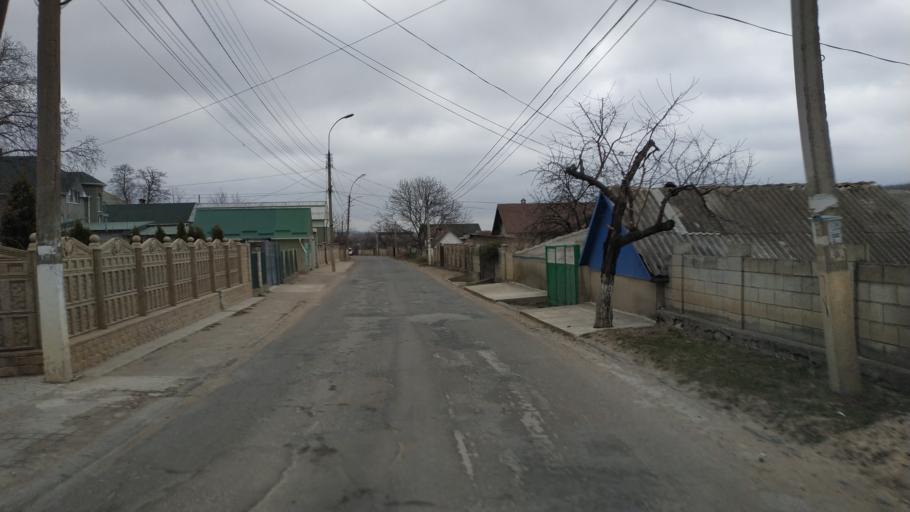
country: MD
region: Laloveni
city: Ialoveni
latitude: 46.9042
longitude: 28.8075
